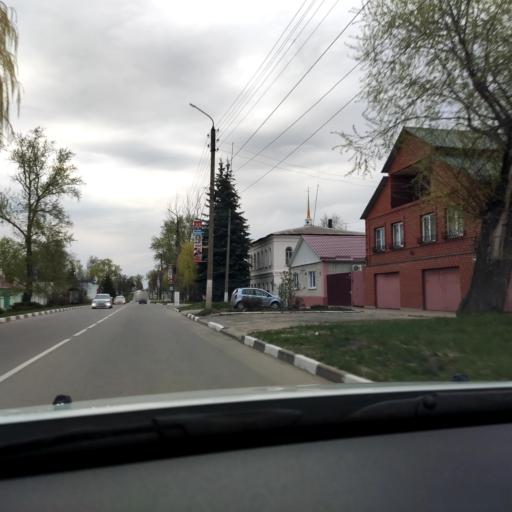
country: RU
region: Lipetsk
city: Zadonsk
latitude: 52.3891
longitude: 38.9148
